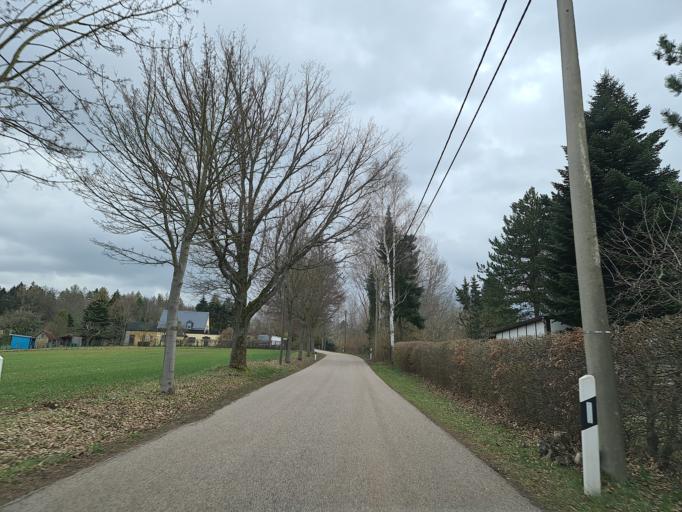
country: DE
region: Saxony
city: Lichtenstein
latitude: 50.7402
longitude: 12.6227
